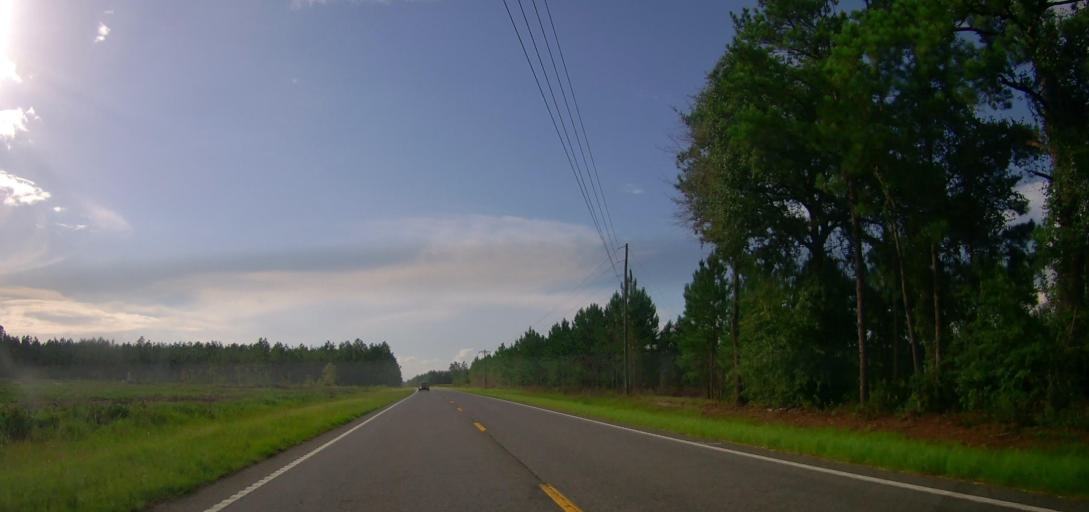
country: US
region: Georgia
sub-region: Coffee County
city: Nicholls
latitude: 31.3568
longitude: -82.6200
